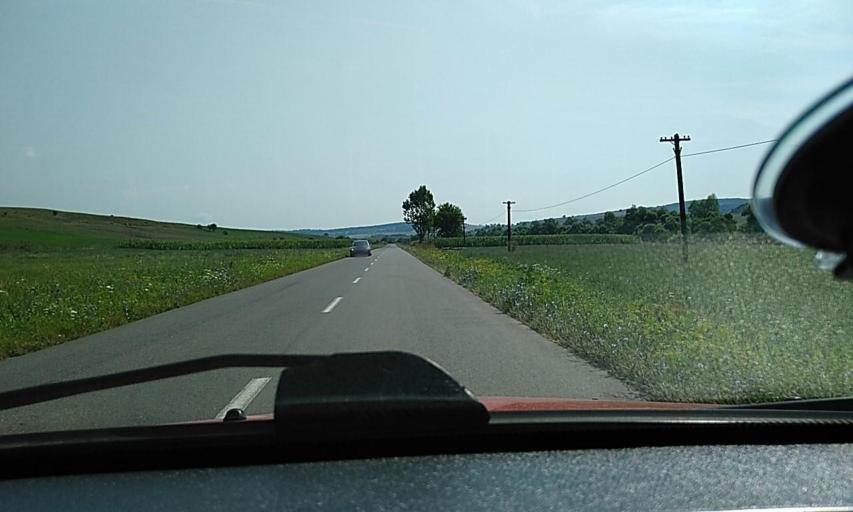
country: RO
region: Brasov
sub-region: Oras Rupea
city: Rupea
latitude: 46.0127
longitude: 25.1589
